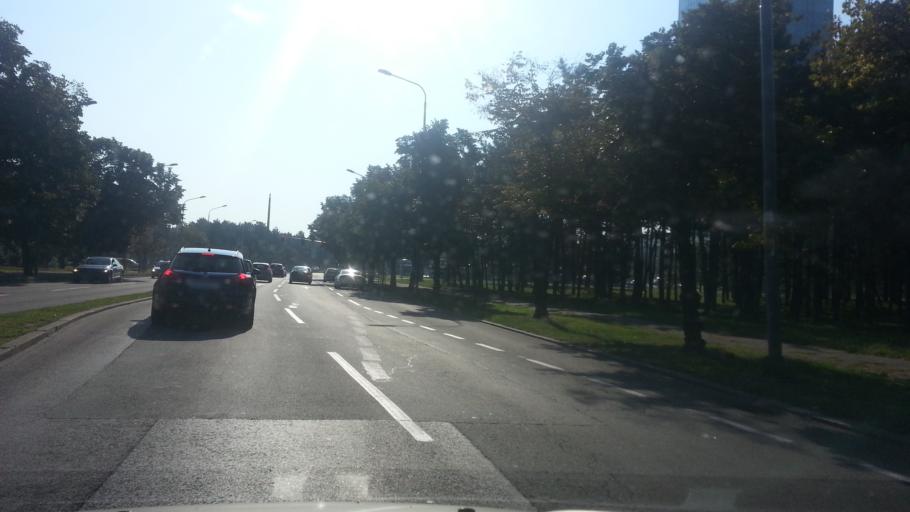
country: RS
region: Central Serbia
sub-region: Belgrade
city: Novi Beograd
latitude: 44.8183
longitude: 20.4358
